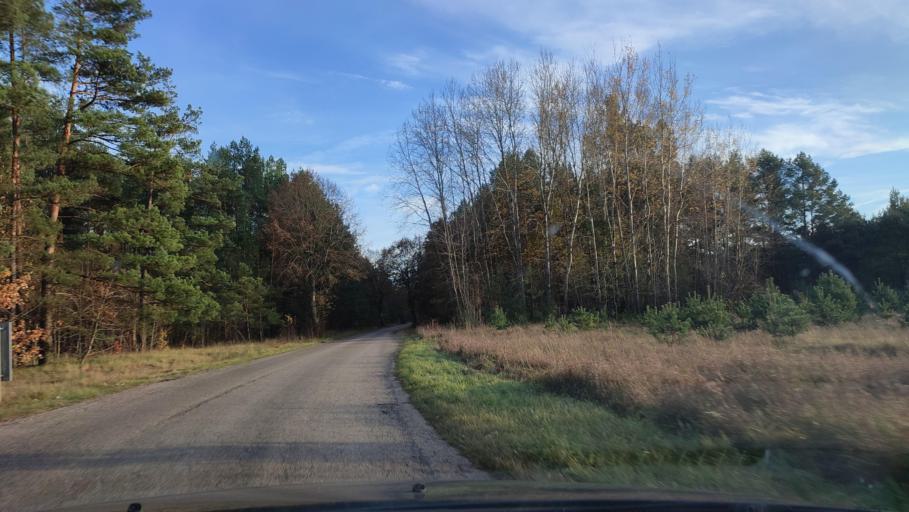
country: PL
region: Warmian-Masurian Voivodeship
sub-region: Powiat szczycienski
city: Jedwabno
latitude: 53.3638
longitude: 20.7296
